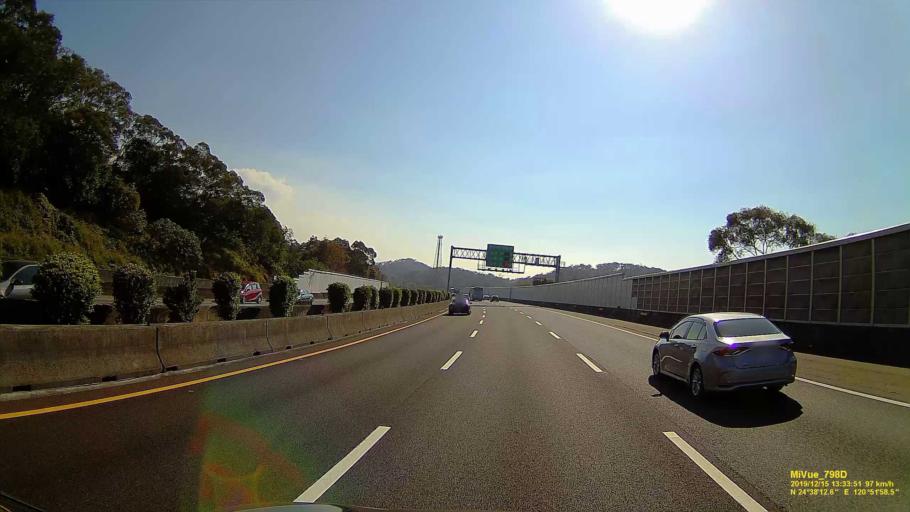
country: TW
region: Taiwan
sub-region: Miaoli
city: Miaoli
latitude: 24.6366
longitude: 120.8661
